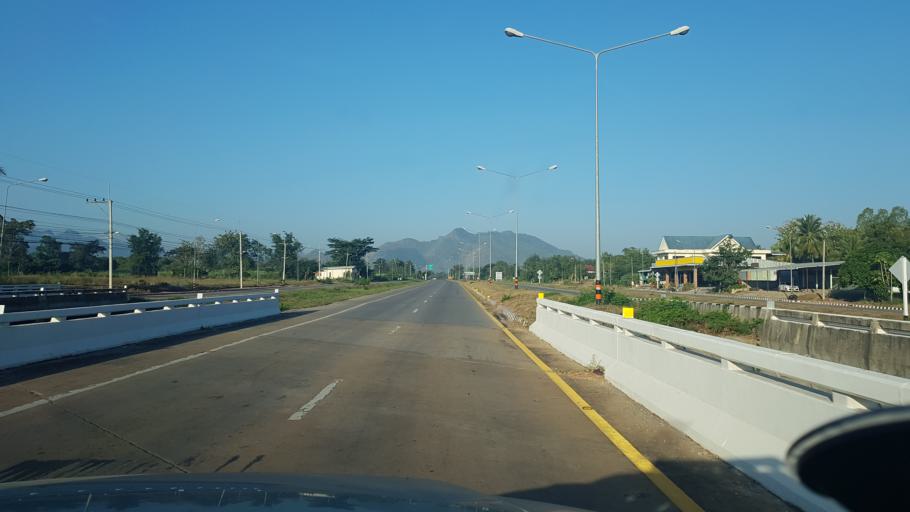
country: TH
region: Chaiyaphum
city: Khon San
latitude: 16.5954
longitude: 101.9251
